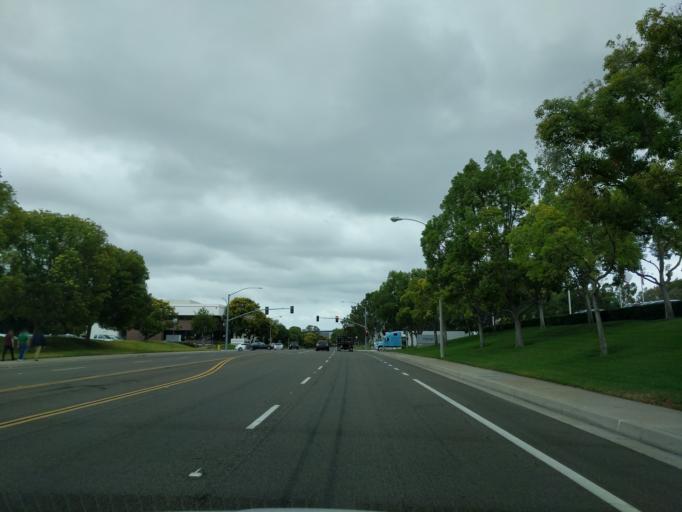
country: US
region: California
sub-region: Orange County
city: Lake Forest
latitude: 33.6433
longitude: -117.7199
